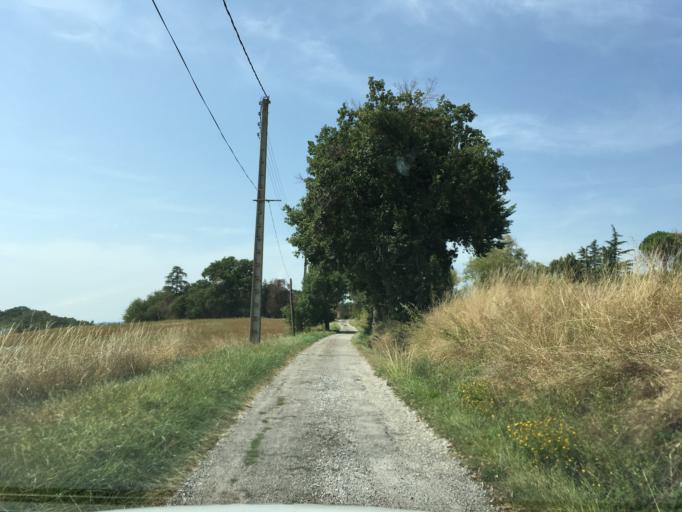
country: FR
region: Midi-Pyrenees
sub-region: Departement du Tarn
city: Castres
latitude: 43.6477
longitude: 2.2317
